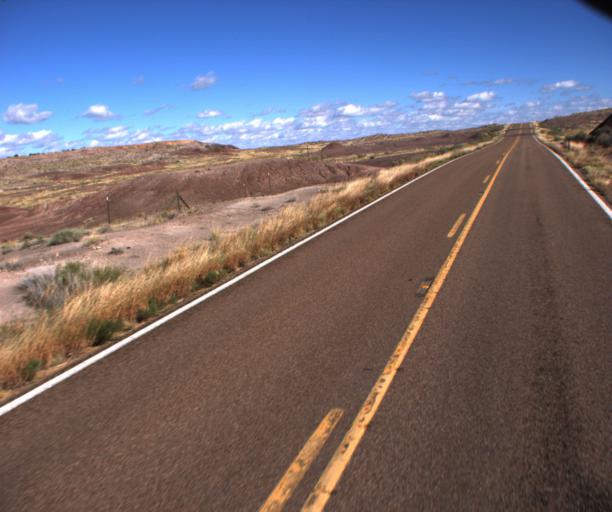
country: US
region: Arizona
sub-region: Apache County
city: Saint Johns
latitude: 34.6549
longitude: -109.2969
